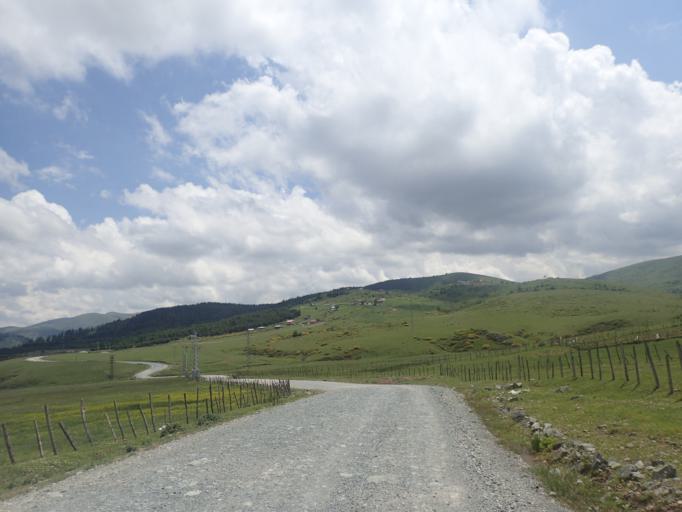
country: TR
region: Ordu
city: Topcam
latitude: 40.6856
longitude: 37.9293
